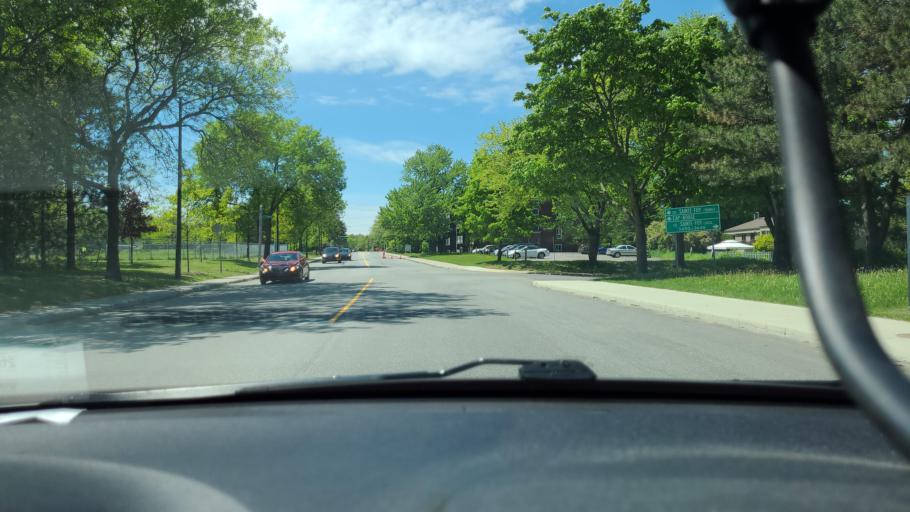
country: CA
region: Quebec
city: L'Ancienne-Lorette
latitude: 46.7676
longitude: -71.3255
